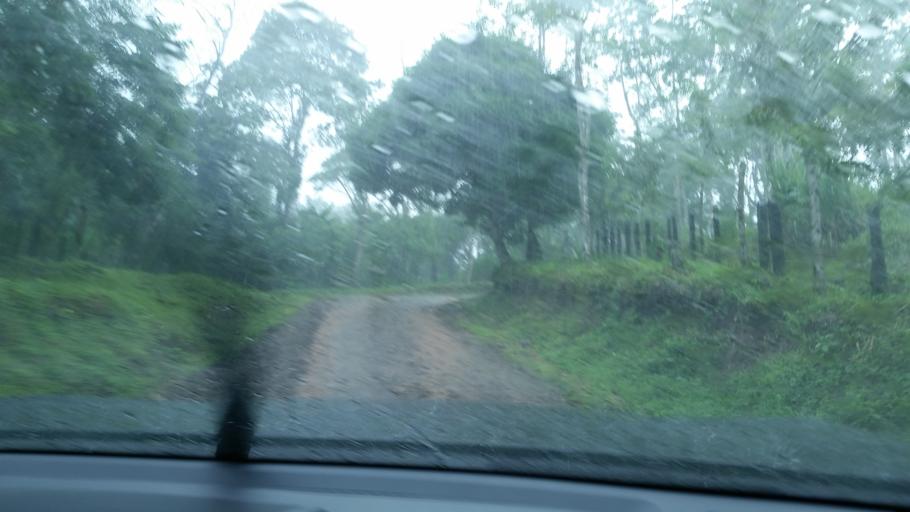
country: NI
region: Atlantico Norte (RAAN)
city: Waslala
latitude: 13.1554
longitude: -85.4310
